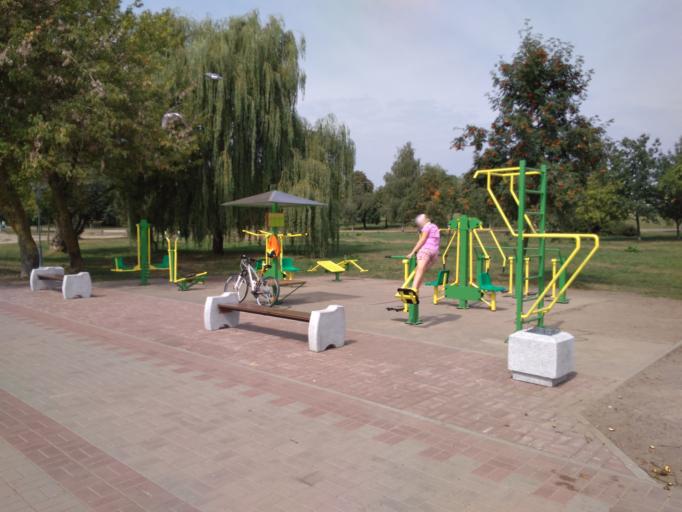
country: BY
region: Brest
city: Brest
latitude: 52.0822
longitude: 23.6958
